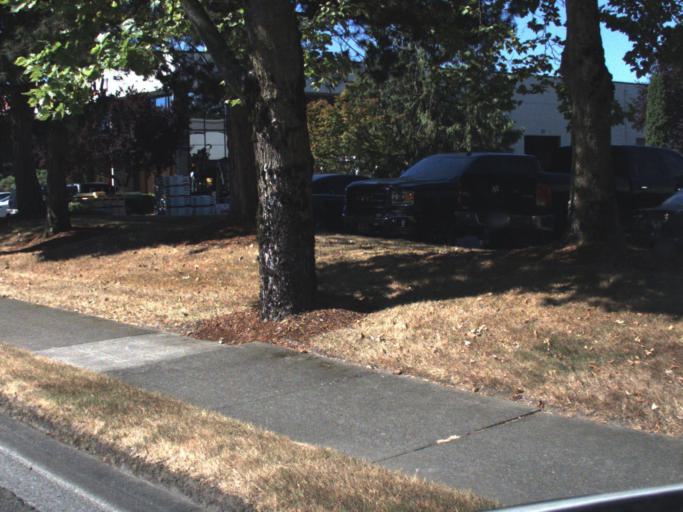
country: US
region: Washington
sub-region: King County
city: Kent
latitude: 47.4047
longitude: -122.2494
